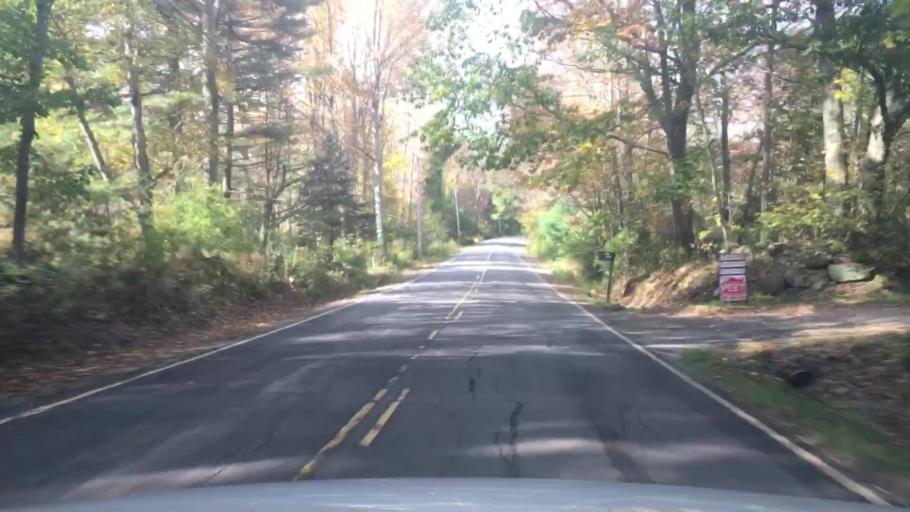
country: US
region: Maine
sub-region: Knox County
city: Union
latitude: 44.1749
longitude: -69.2551
